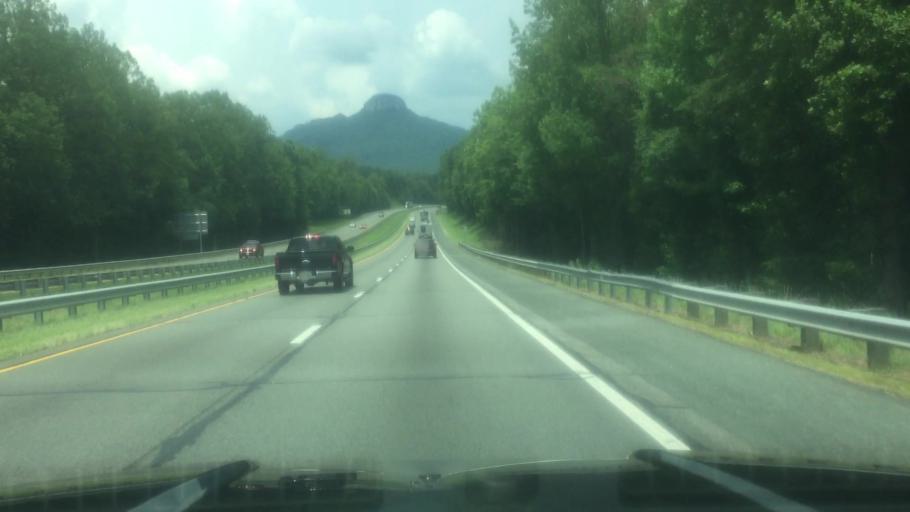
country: US
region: North Carolina
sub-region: Surry County
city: Pilot Mountain
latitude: 36.3203
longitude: -80.4430
